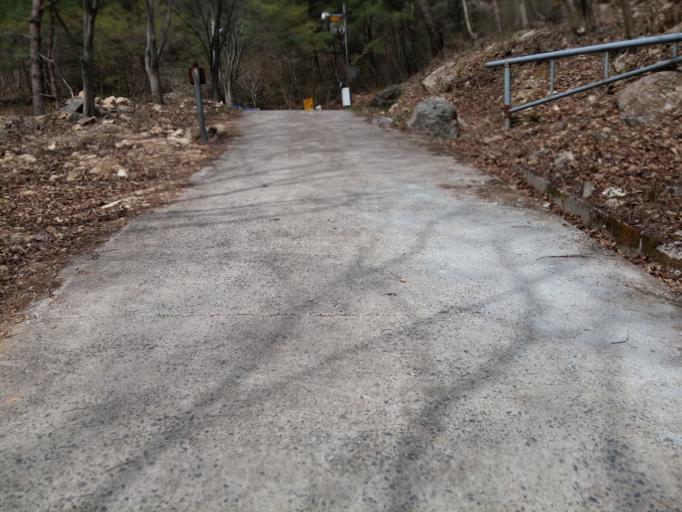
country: KR
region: Chungcheongbuk-do
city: Okcheon
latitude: 36.2429
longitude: 127.5565
